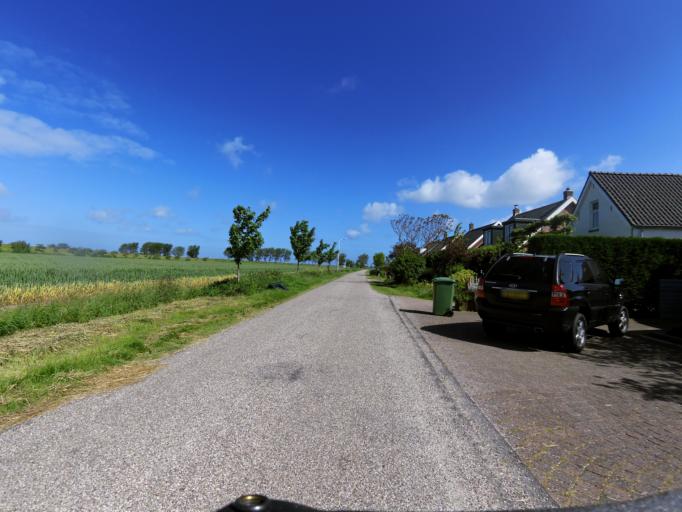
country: NL
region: Zeeland
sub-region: Schouwen-Duiveland
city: Scharendijke
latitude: 51.6901
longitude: 3.9250
